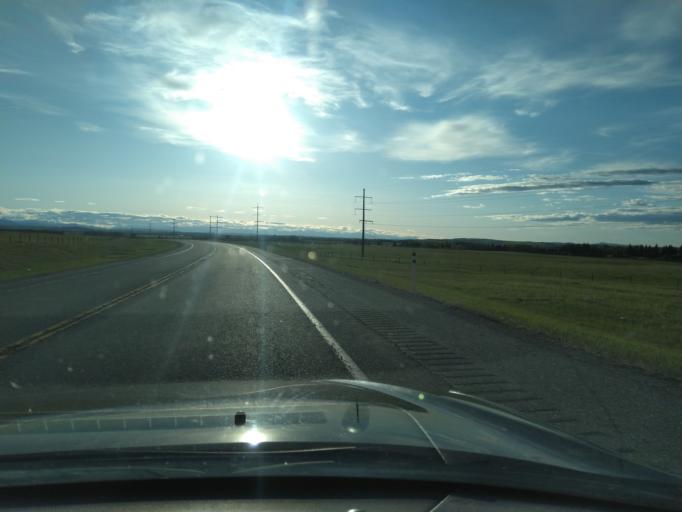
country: CA
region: Alberta
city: Cochrane
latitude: 51.0230
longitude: -114.3327
